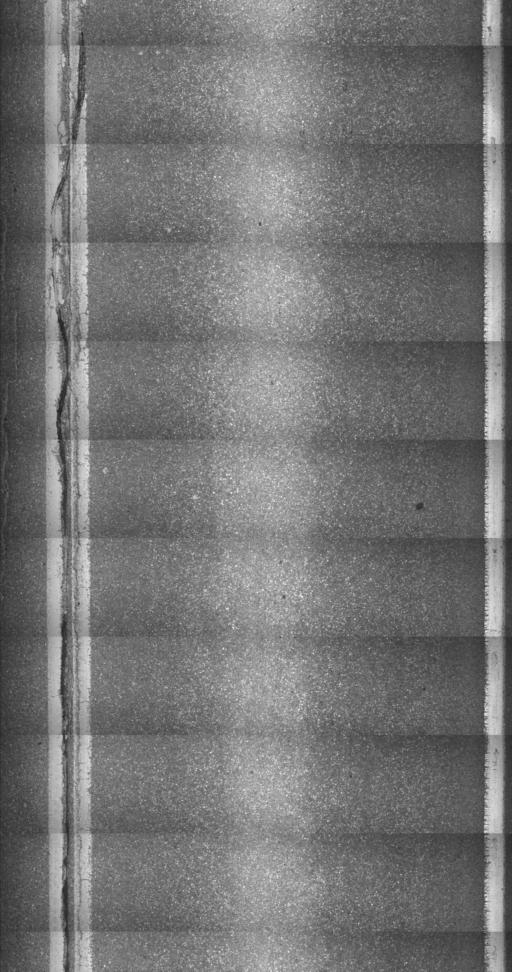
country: US
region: Vermont
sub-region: Chittenden County
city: Hinesburg
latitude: 44.3831
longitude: -73.1266
